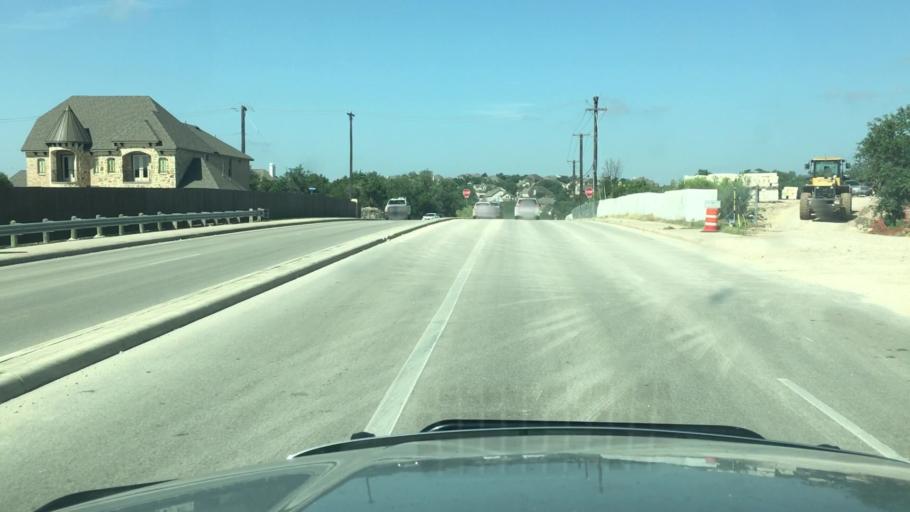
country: US
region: Texas
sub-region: Bexar County
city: Timberwood Park
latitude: 29.6697
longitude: -98.4568
